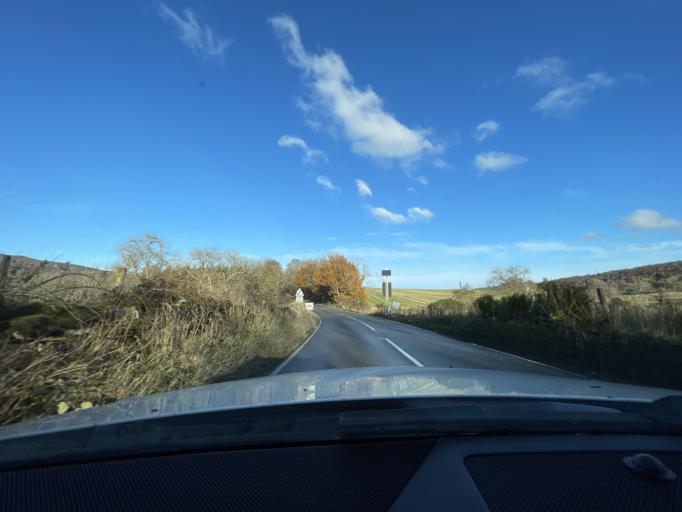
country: GB
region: Scotland
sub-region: Highland
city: Inverness
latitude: 57.3970
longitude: -4.3195
